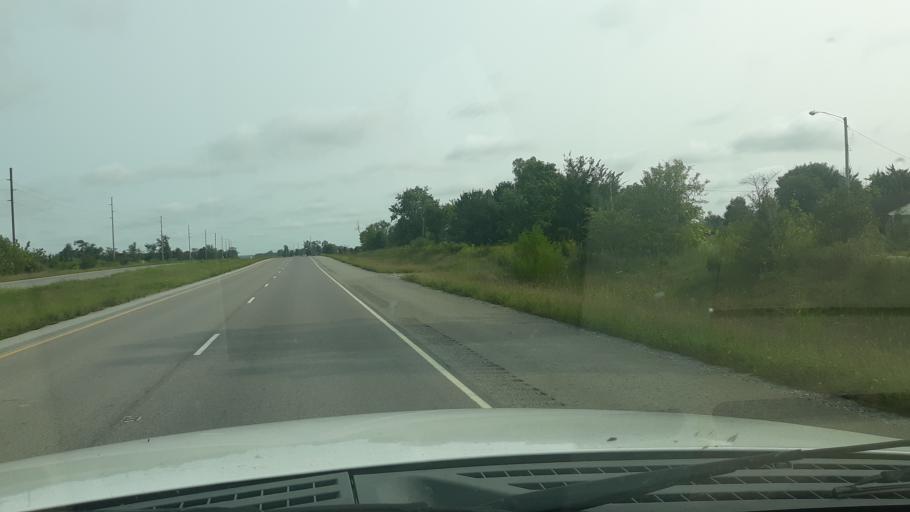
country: US
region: Illinois
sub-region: Saline County
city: Eldorado
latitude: 37.8276
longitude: -88.4238
